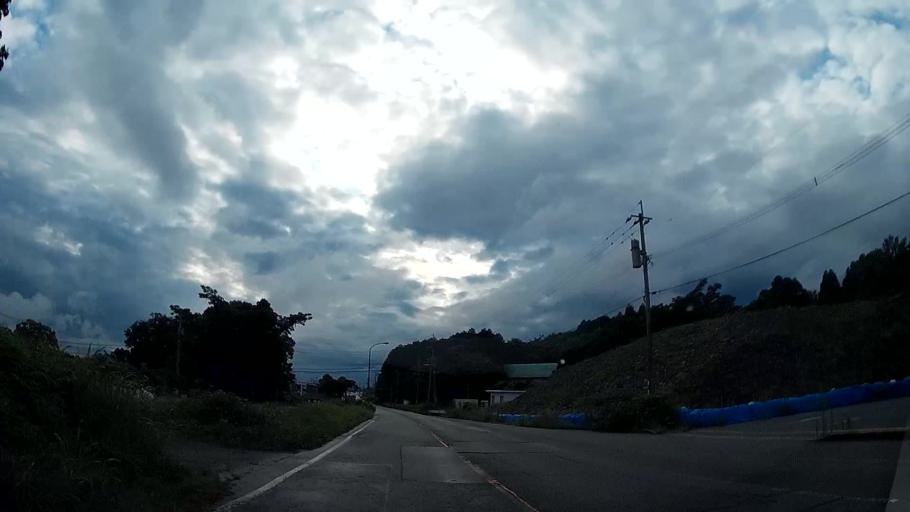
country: JP
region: Kumamoto
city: Ozu
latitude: 32.8795
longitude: 130.9087
